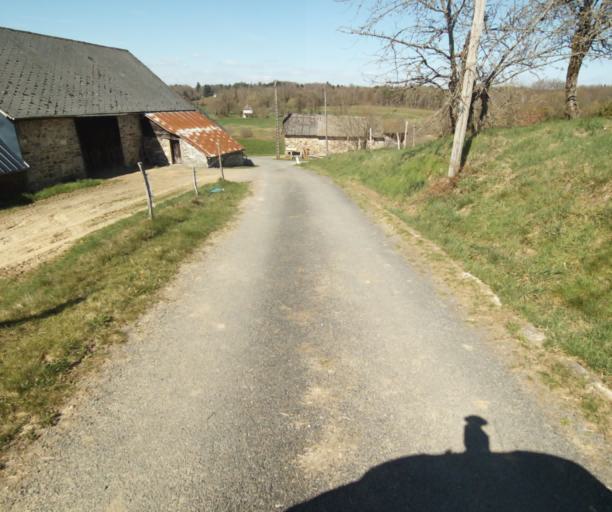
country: FR
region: Limousin
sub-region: Departement de la Correze
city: Saint-Mexant
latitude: 45.2980
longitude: 1.6828
